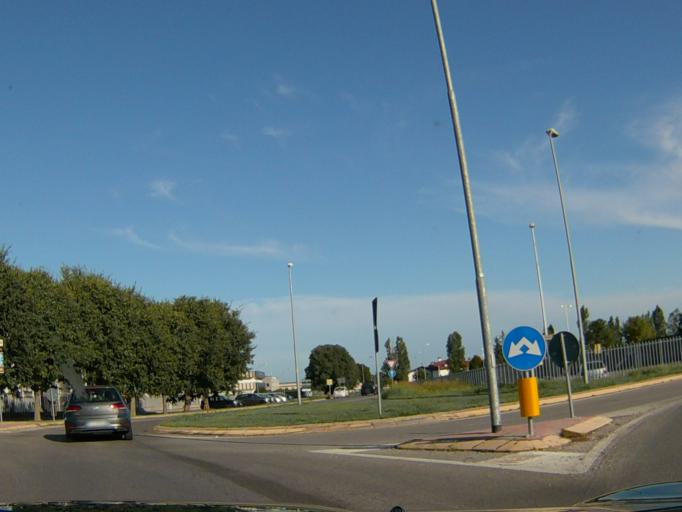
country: IT
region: Lombardy
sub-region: Provincia di Brescia
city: Molinetto
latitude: 45.4936
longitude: 10.3590
